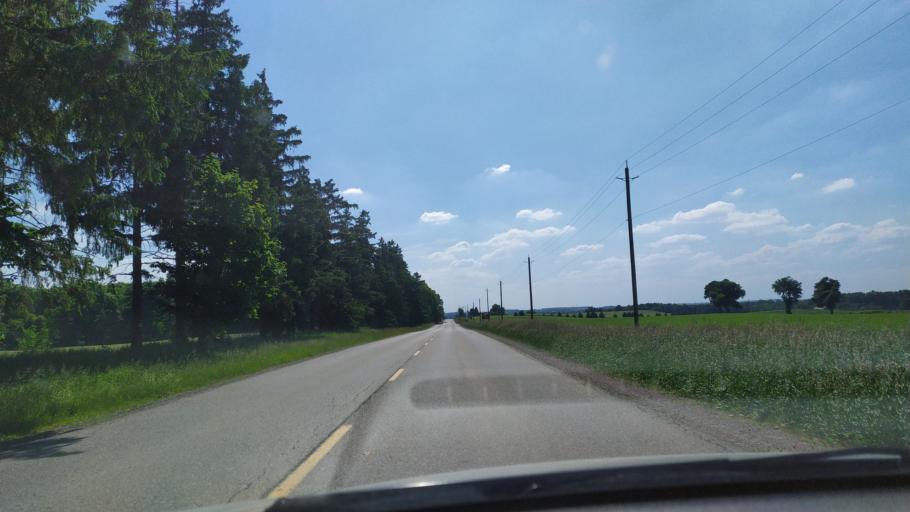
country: CA
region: Ontario
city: Kitchener
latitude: 43.3636
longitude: -80.6088
